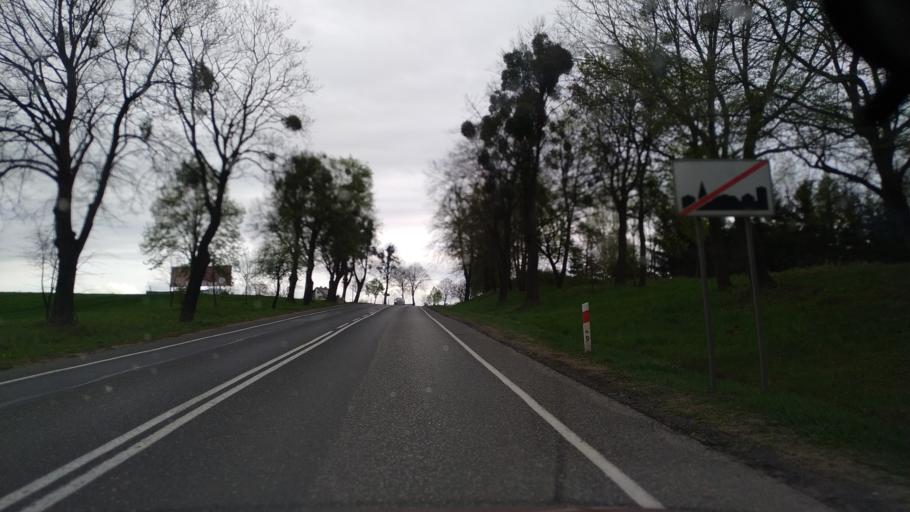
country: PL
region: Pomeranian Voivodeship
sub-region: Powiat starogardzki
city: Starogard Gdanski
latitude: 53.9476
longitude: 18.4693
